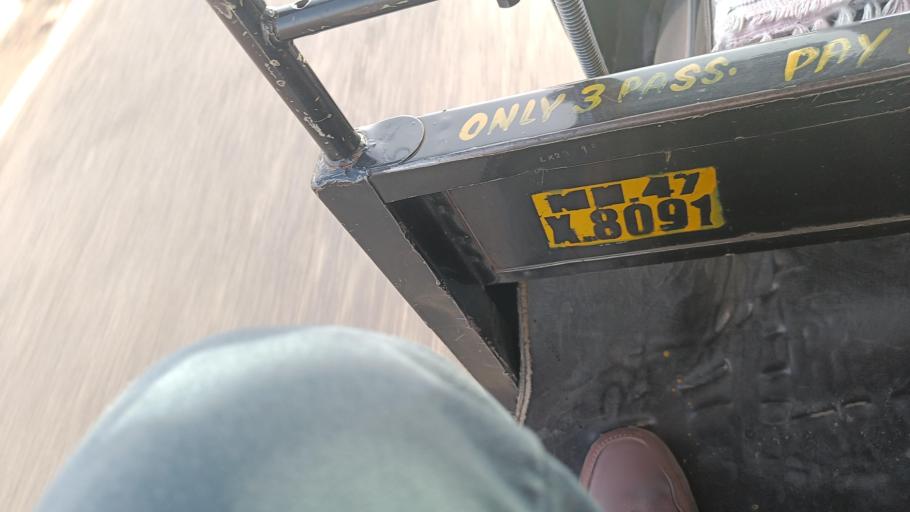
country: IN
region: Maharashtra
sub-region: Mumbai Suburban
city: Mumbai
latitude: 19.0497
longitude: 72.8375
